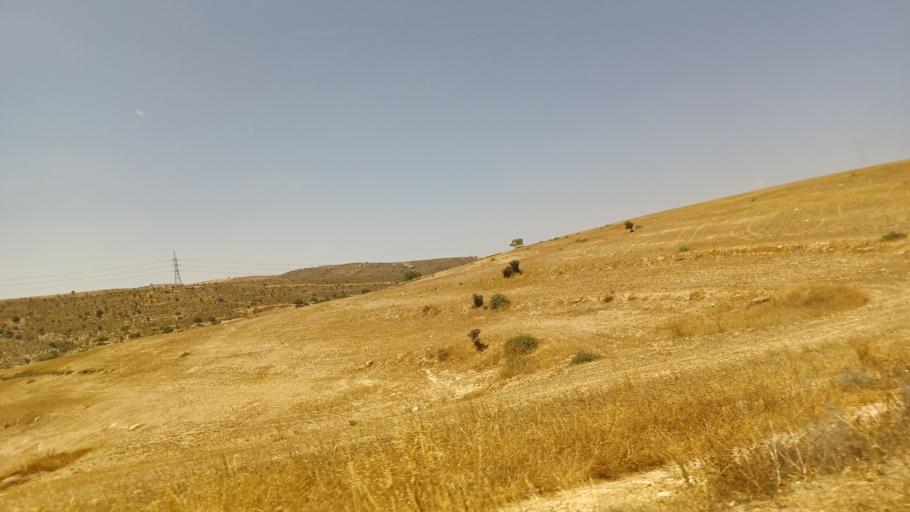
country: CY
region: Lefkosia
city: Lympia
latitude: 34.9919
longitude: 33.4810
